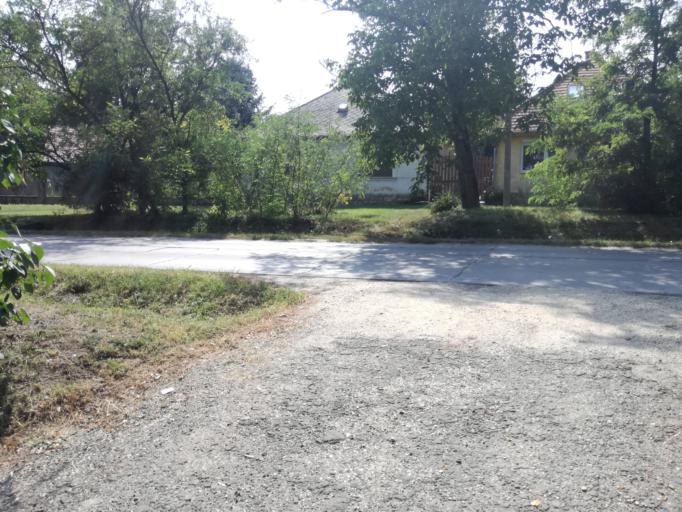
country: HU
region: Pest
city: Erd
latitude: 47.3673
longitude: 18.9257
